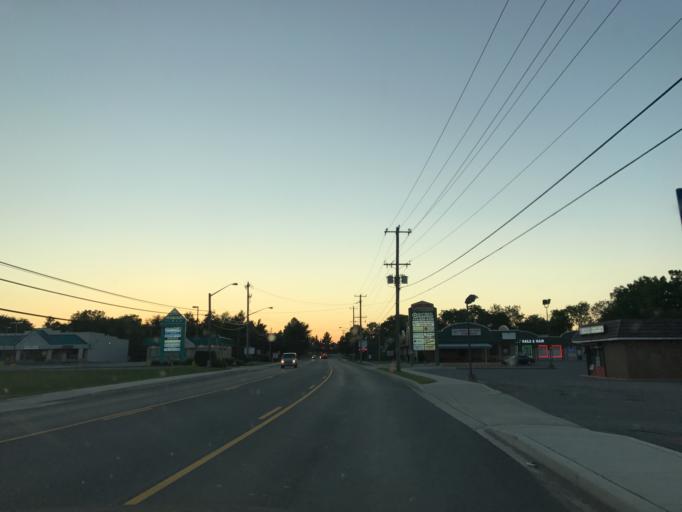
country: US
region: Maryland
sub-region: Cecil County
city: Elkton
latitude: 39.6039
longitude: -75.8300
